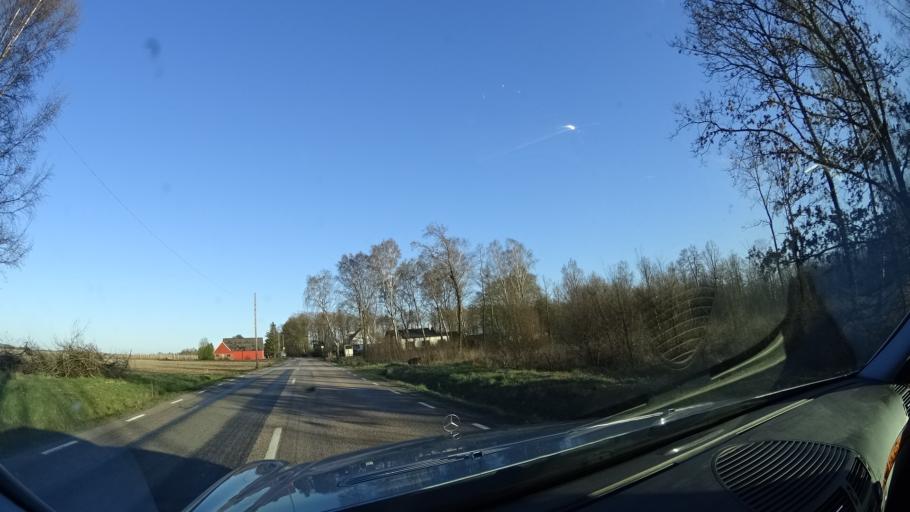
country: SE
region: Skane
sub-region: Bjuvs Kommun
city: Billesholm
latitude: 56.0338
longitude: 13.0304
